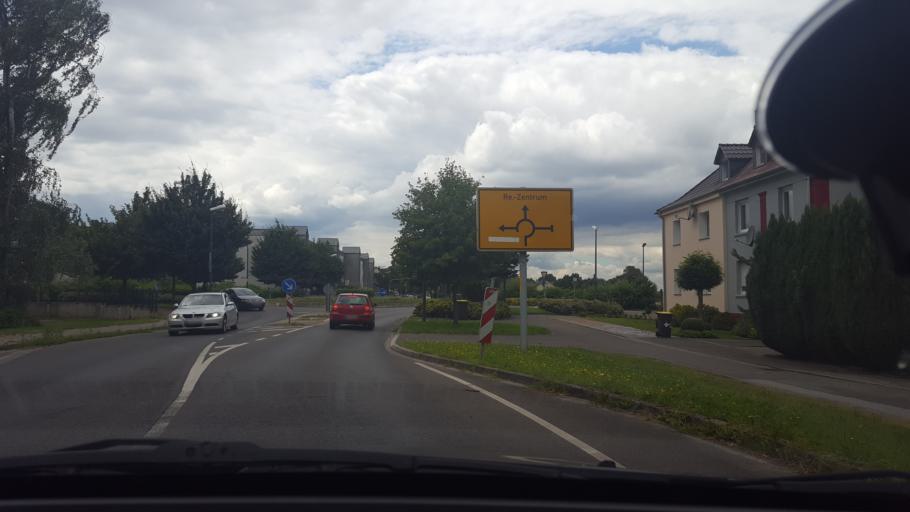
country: DE
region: North Rhine-Westphalia
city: Oer-Erkenschwick
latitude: 51.6243
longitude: 7.2354
